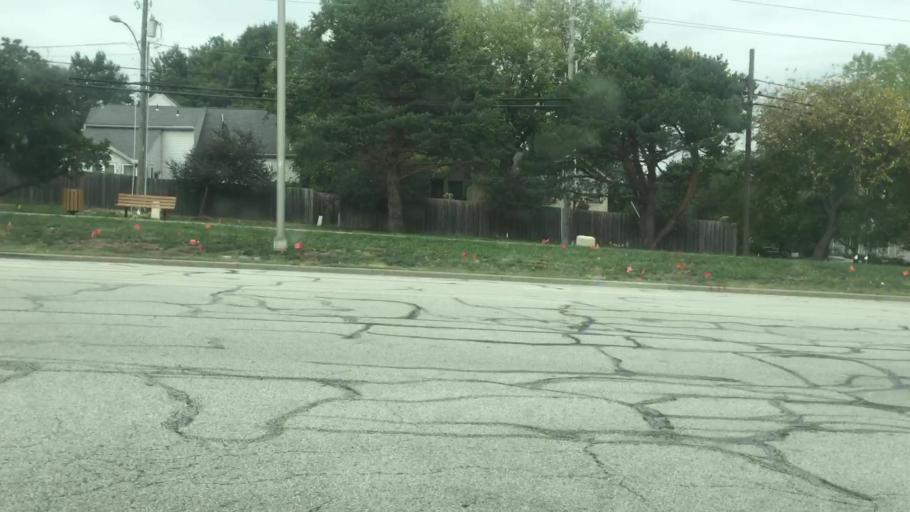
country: US
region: Kansas
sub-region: Johnson County
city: Lenexa
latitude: 38.9562
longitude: -94.7550
